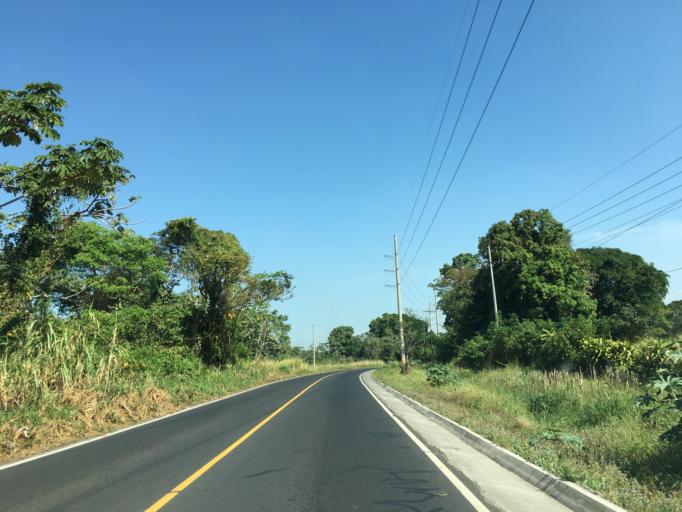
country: GT
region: Escuintla
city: Siquinala
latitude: 14.2817
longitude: -90.9683
